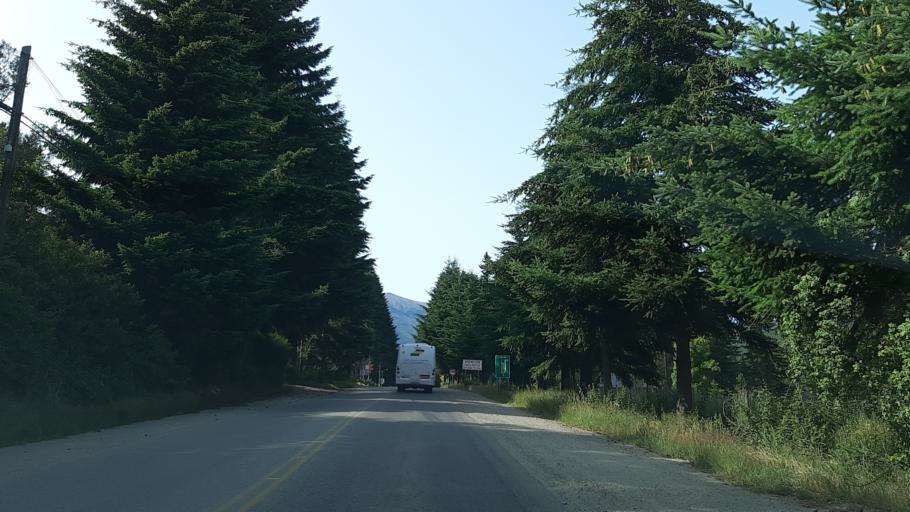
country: AR
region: Rio Negro
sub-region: Departamento de Bariloche
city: San Carlos de Bariloche
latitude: -41.1575
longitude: -71.4081
